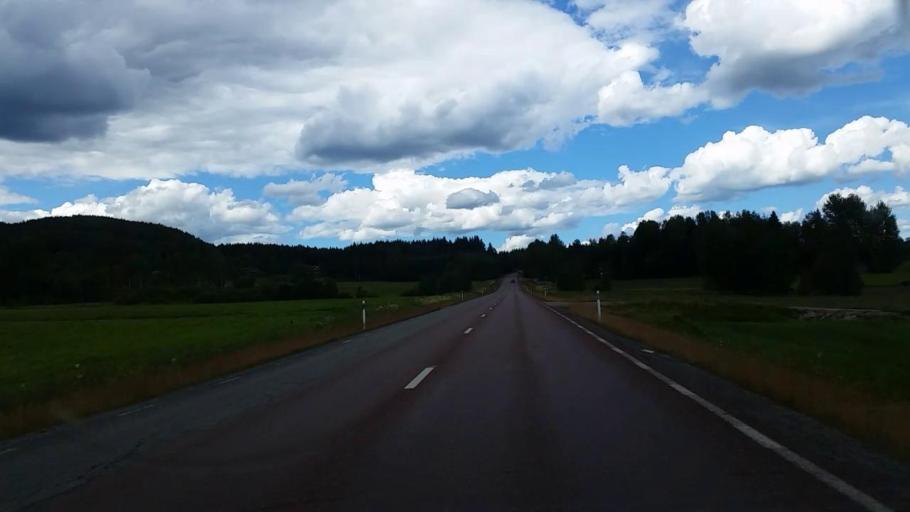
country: SE
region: Gaevleborg
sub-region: Ljusdals Kommun
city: Jaervsoe
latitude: 61.6782
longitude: 16.1453
